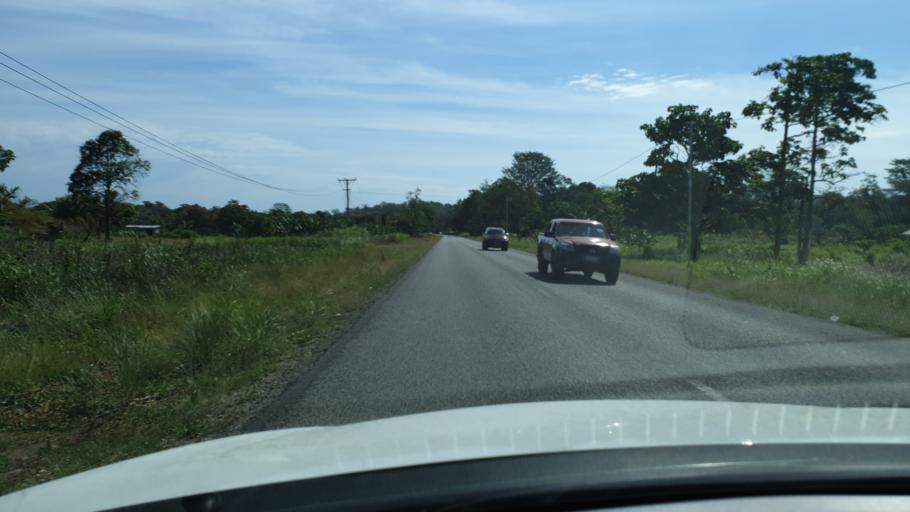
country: PG
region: National Capital
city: Port Moresby
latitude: -9.5508
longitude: 147.3556
